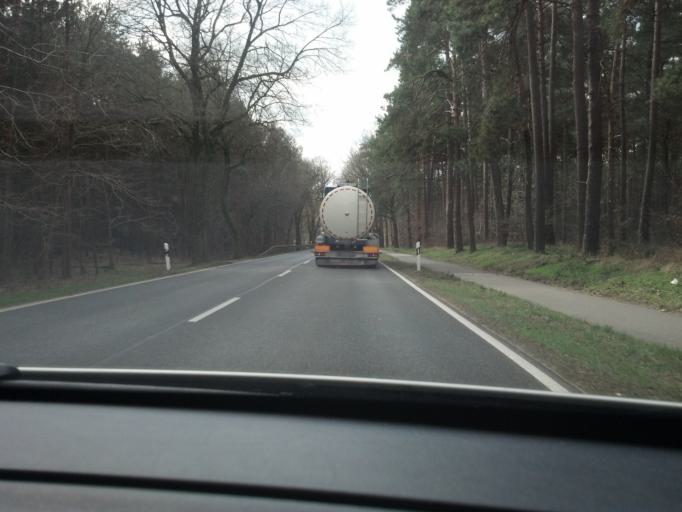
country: DE
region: Mecklenburg-Vorpommern
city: Wesenberg
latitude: 53.2774
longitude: 12.9294
